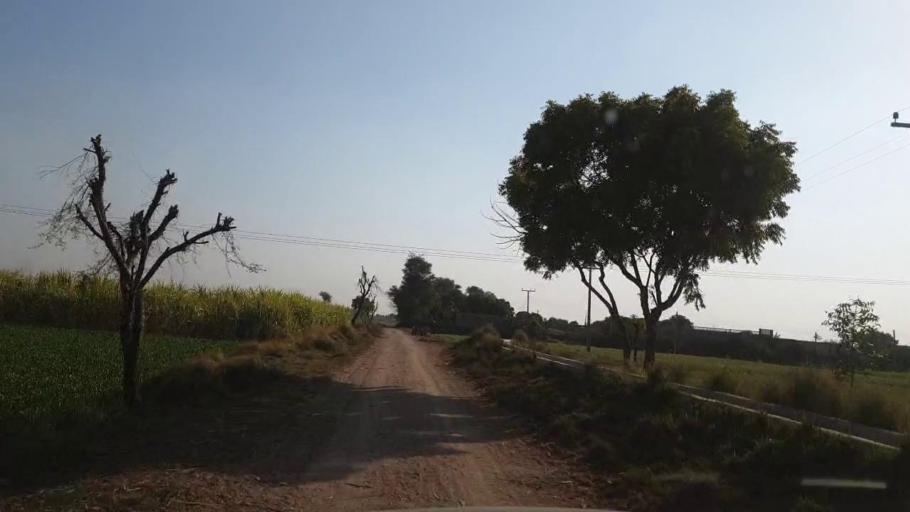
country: PK
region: Sindh
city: Tando Allahyar
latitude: 25.5672
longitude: 68.6506
